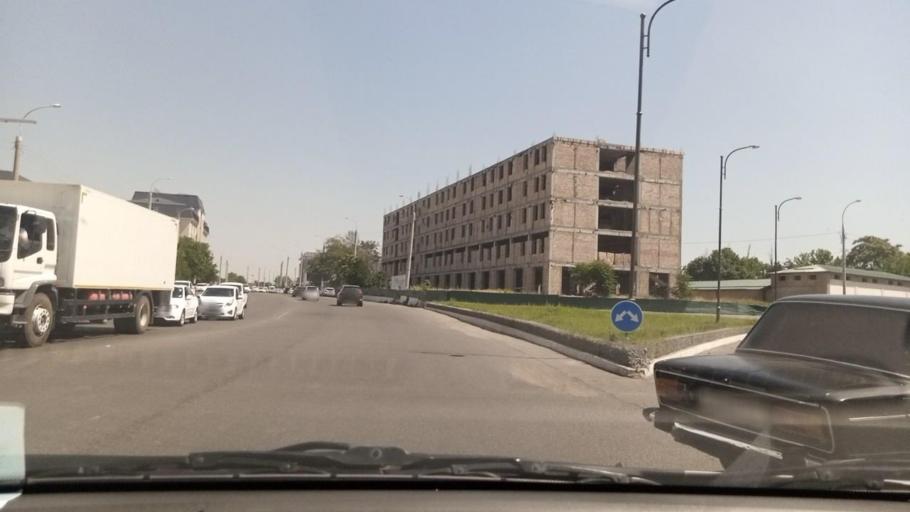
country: UZ
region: Toshkent Shahri
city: Tashkent
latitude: 41.2596
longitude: 69.1884
